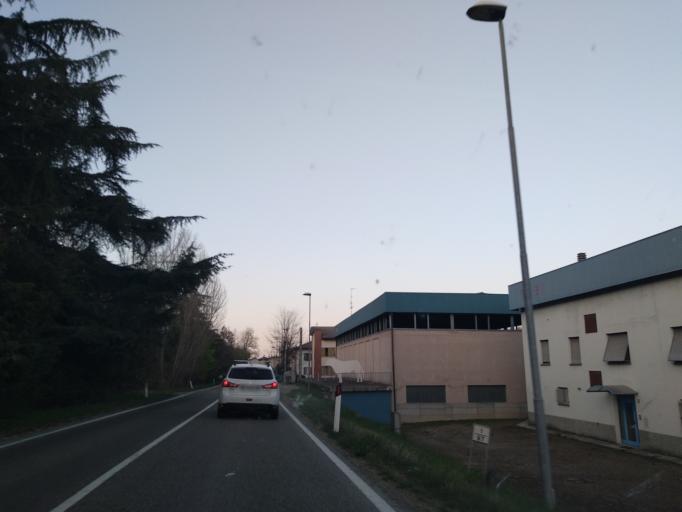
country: IT
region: Emilia-Romagna
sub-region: Provincia di Reggio Emilia
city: Vezzano sul Crostolo
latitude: 44.5924
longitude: 10.5382
